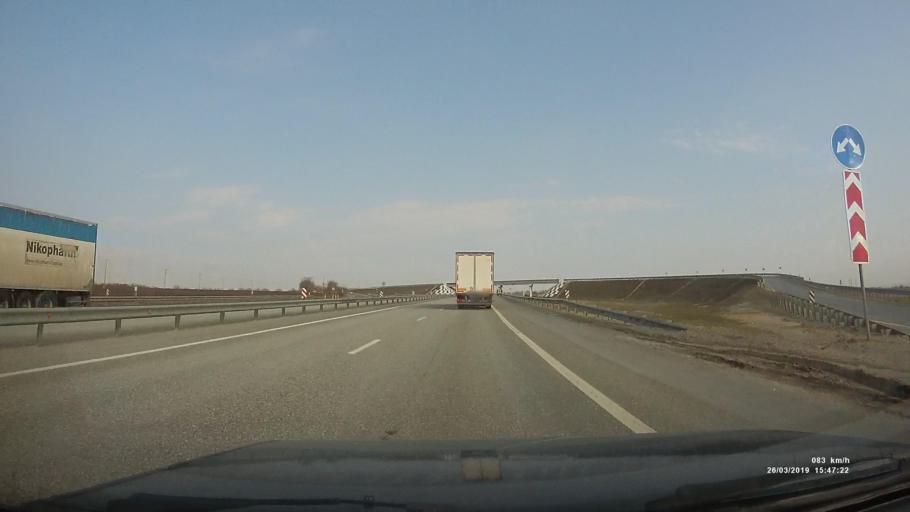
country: RU
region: Rostov
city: Chaltyr
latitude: 47.2824
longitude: 39.4371
